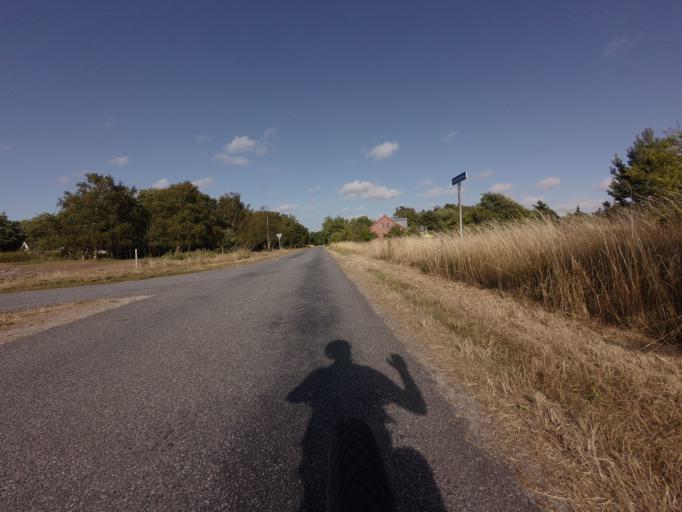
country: DK
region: North Denmark
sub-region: Laeso Kommune
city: Byrum
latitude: 57.2699
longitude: 10.9338
